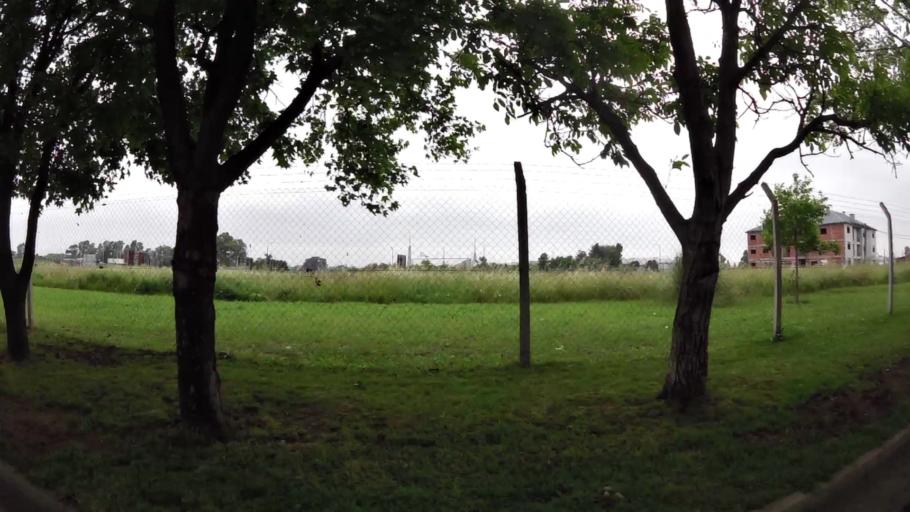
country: AR
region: Buenos Aires
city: San Justo
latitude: -34.7264
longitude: -58.5185
